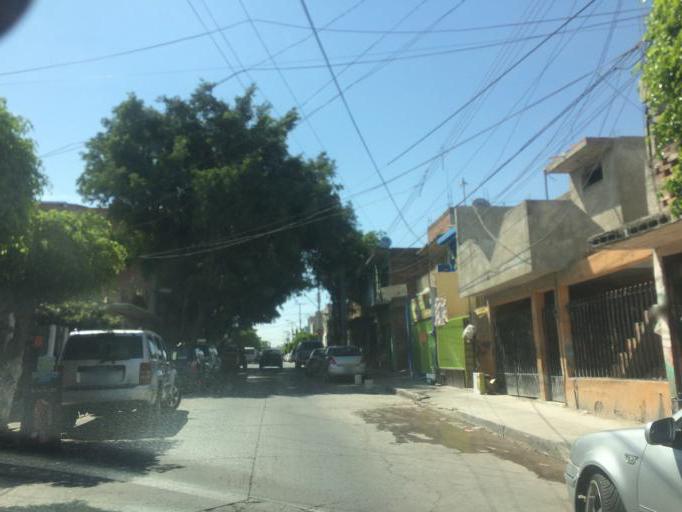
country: MX
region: Guanajuato
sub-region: Leon
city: La Ermita
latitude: 21.1359
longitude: -101.7082
